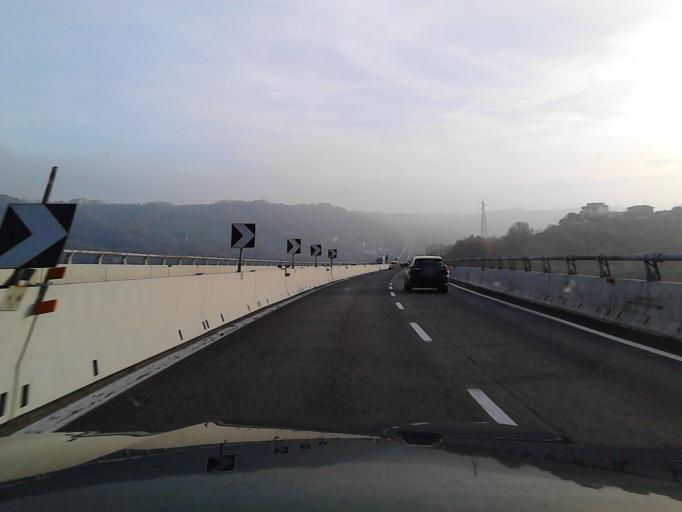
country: IT
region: Abruzzo
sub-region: Provincia di Chieti
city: San Vito Chietino
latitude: 42.2957
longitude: 14.4329
